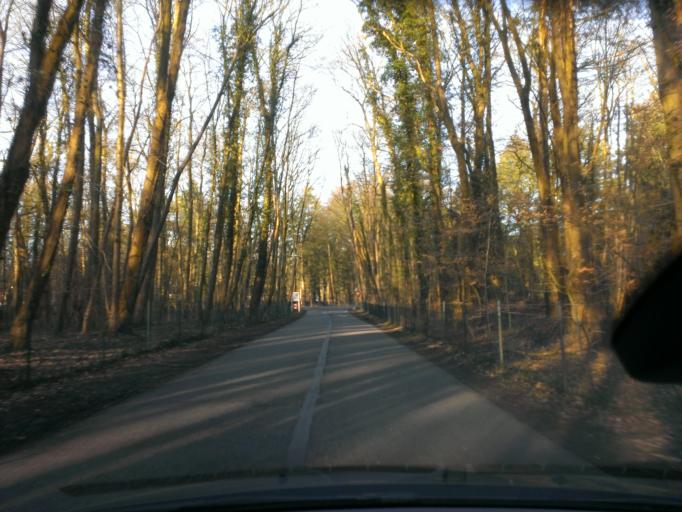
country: NL
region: Gelderland
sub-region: Gemeente Heerde
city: Heerde
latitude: 52.4244
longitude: 6.0640
